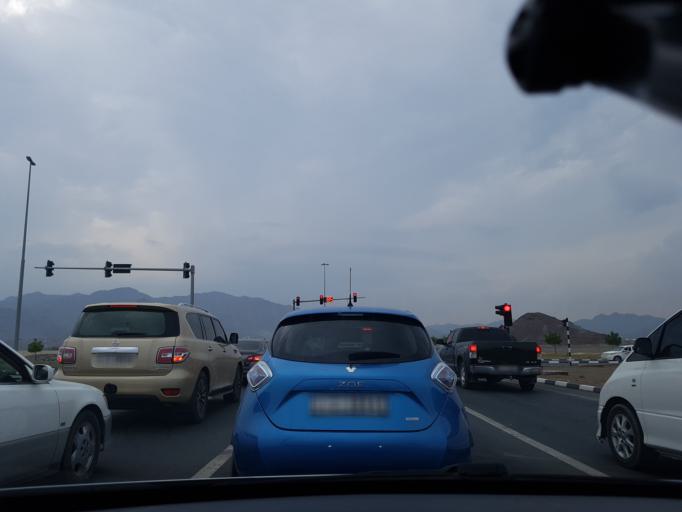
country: AE
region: Al Fujayrah
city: Al Fujayrah
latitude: 25.1231
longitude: 56.2828
